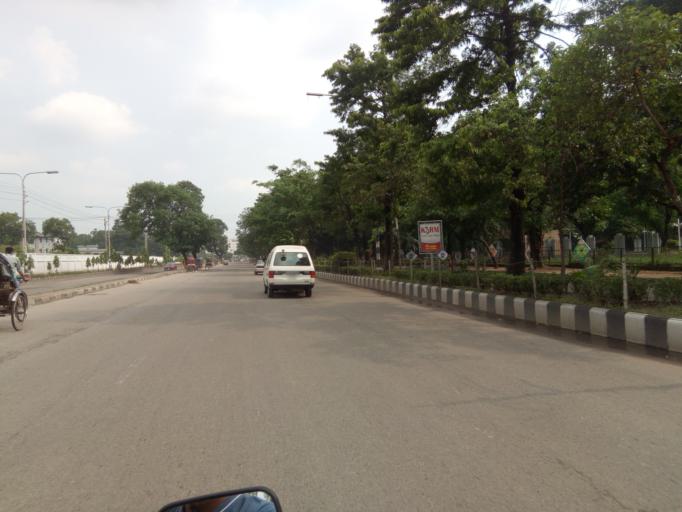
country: BD
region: Dhaka
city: Azimpur
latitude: 23.7692
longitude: 90.3828
